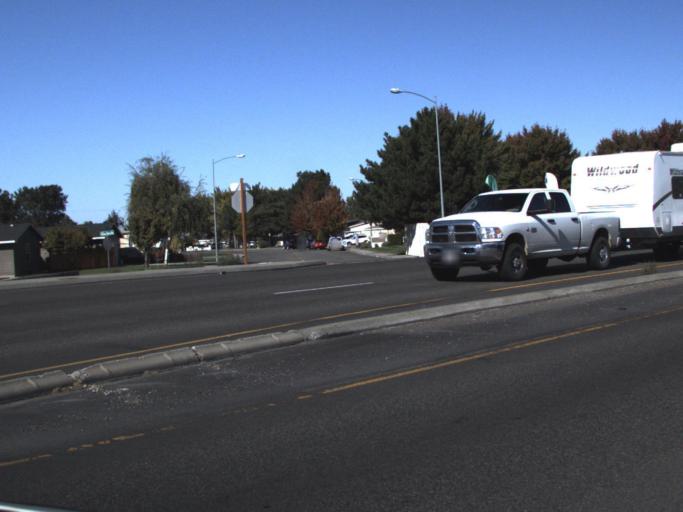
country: US
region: Washington
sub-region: Benton County
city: Kennewick
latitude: 46.2139
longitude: -119.1582
